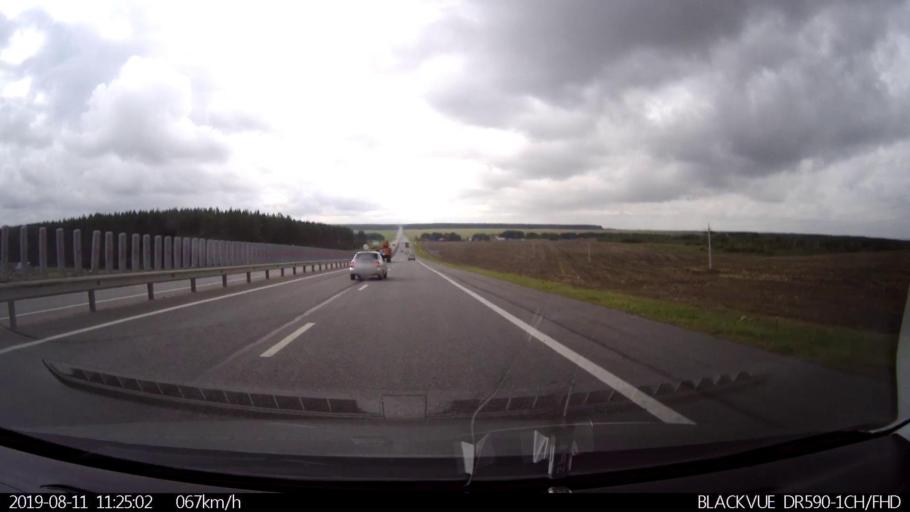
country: RU
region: Ulyanovsk
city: Krasnyy Gulyay
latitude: 54.1214
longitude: 48.2394
